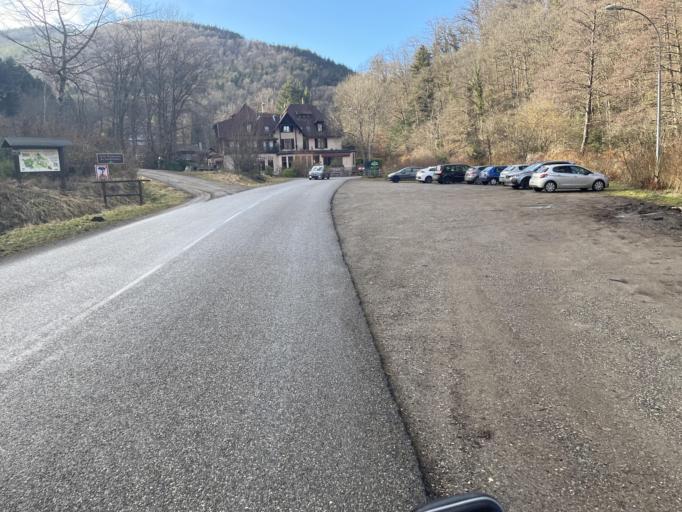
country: FR
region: Alsace
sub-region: Departement du Haut-Rhin
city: Buhl
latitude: 47.9209
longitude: 7.1718
